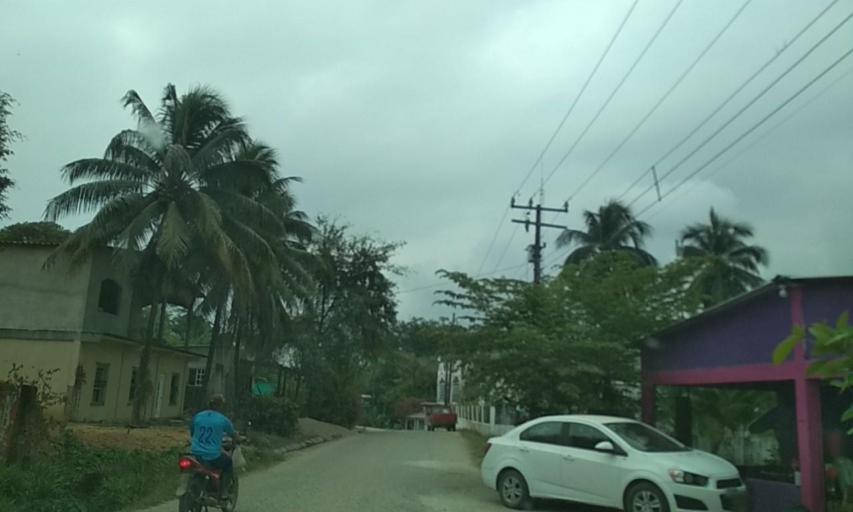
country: MX
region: Veracruz
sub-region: Uxpanapa
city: Poblado 10
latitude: 17.4528
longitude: -94.0989
